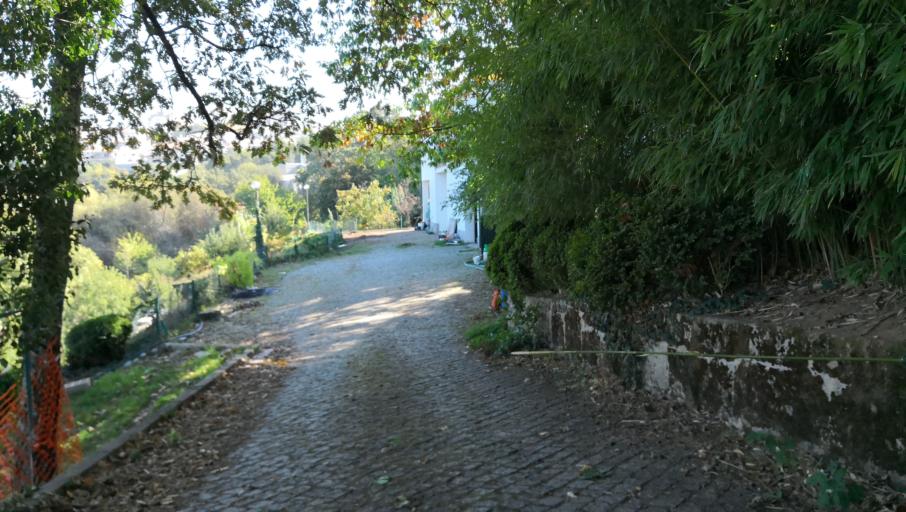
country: PT
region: Vila Real
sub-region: Vila Real
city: Vila Real
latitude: 41.3044
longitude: -7.7309
